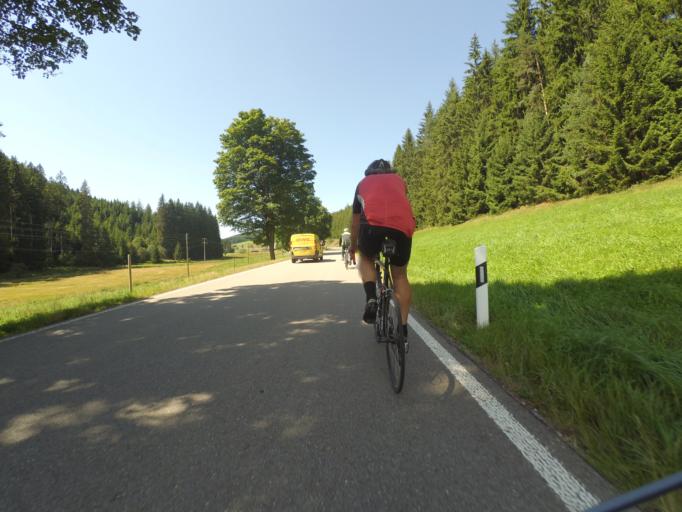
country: DE
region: Baden-Wuerttemberg
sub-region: Freiburg Region
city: Eisenbach
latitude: 47.9788
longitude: 8.2787
